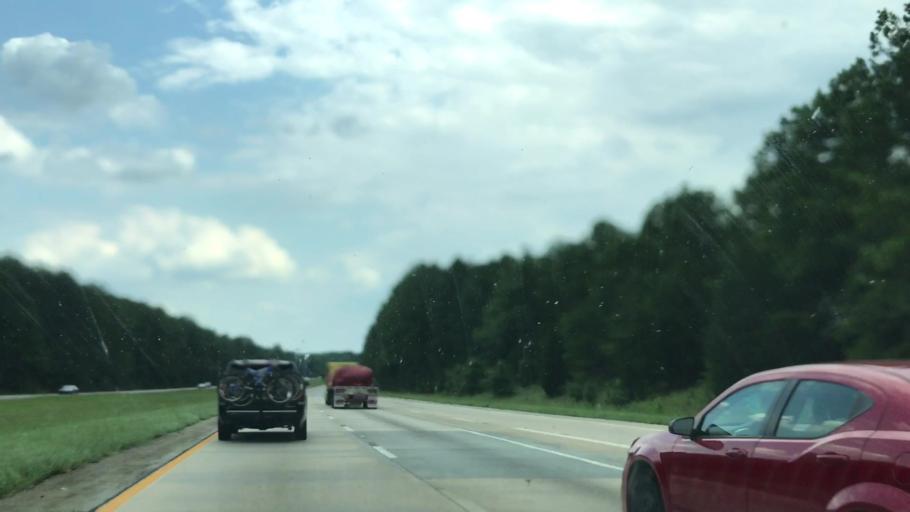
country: US
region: South Carolina
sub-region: Richland County
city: Blythewood
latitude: 34.3037
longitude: -80.9984
